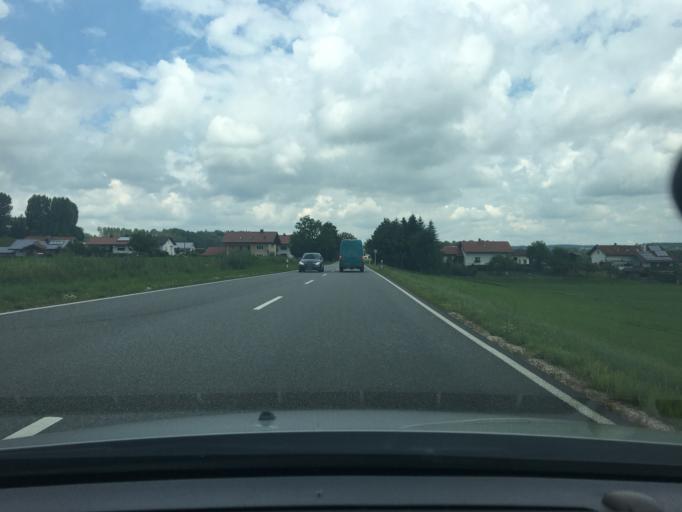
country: DE
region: Bavaria
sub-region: Upper Bavaria
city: Traunreut
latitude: 47.9552
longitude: 12.5686
